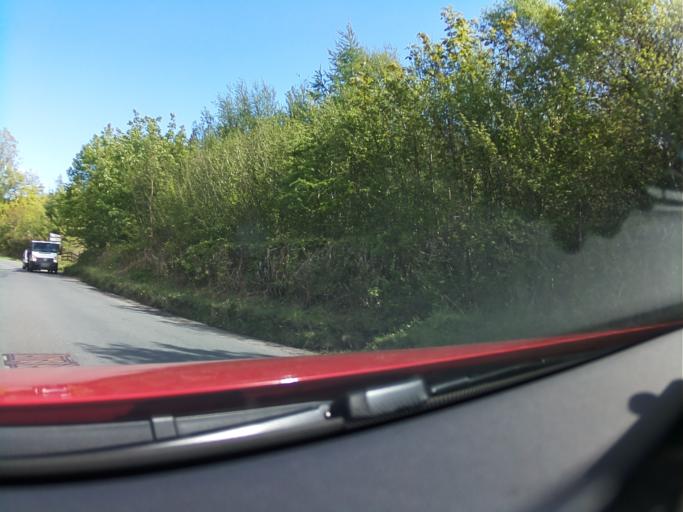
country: GB
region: Wales
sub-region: Caerphilly County Borough
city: Bedwas
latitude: 51.5686
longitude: -3.1887
